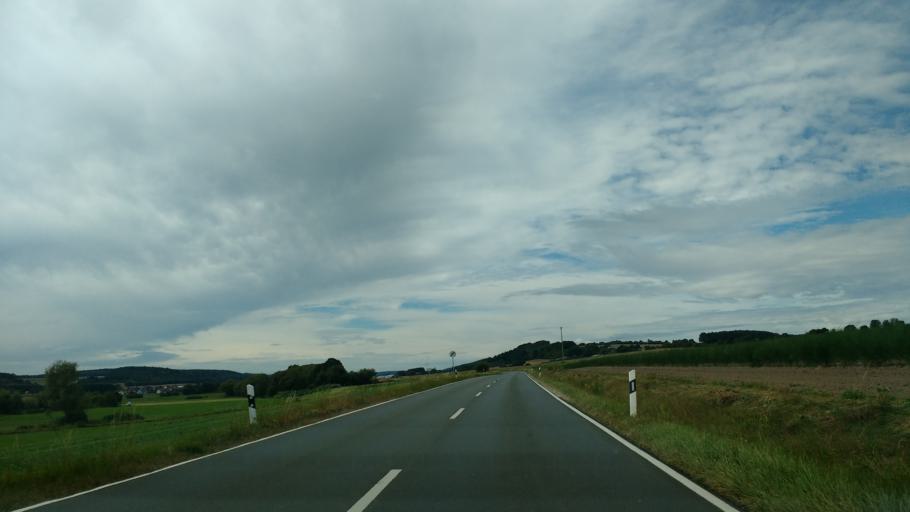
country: DE
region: Bavaria
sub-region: Upper Franconia
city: Schlusselfeld
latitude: 49.7636
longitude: 10.5966
